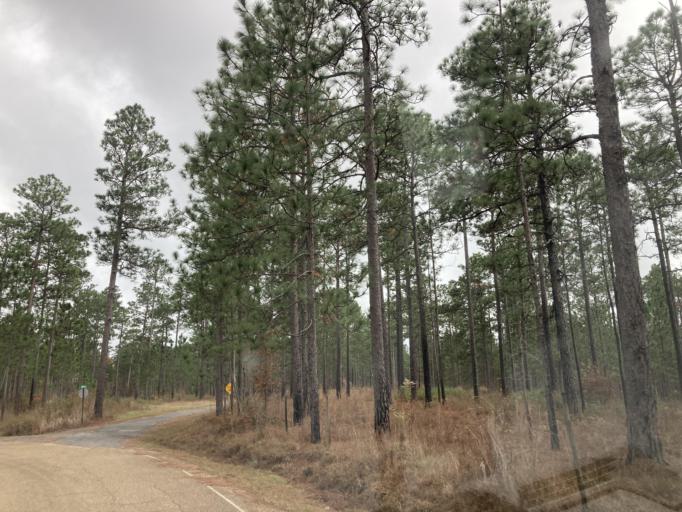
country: US
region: Mississippi
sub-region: Lamar County
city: Lumberton
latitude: 31.0970
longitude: -89.5344
